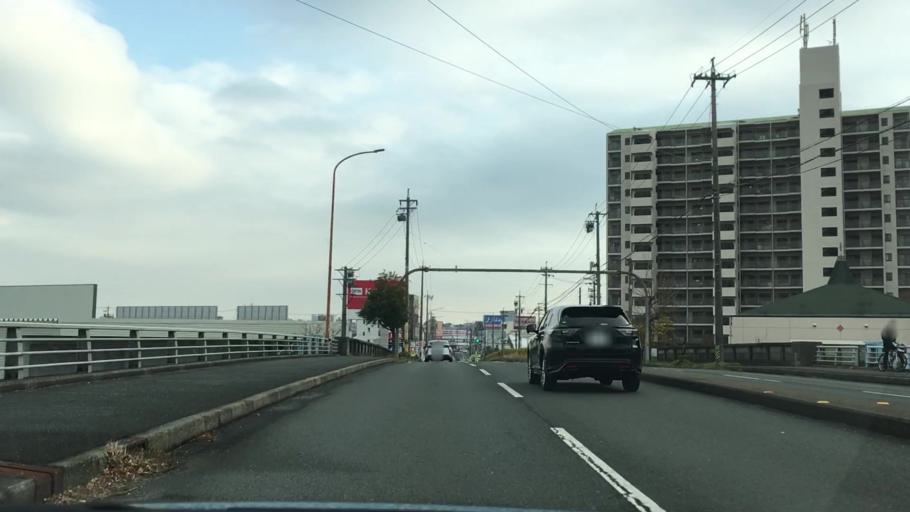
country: JP
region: Aichi
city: Toyohashi
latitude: 34.7527
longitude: 137.3739
